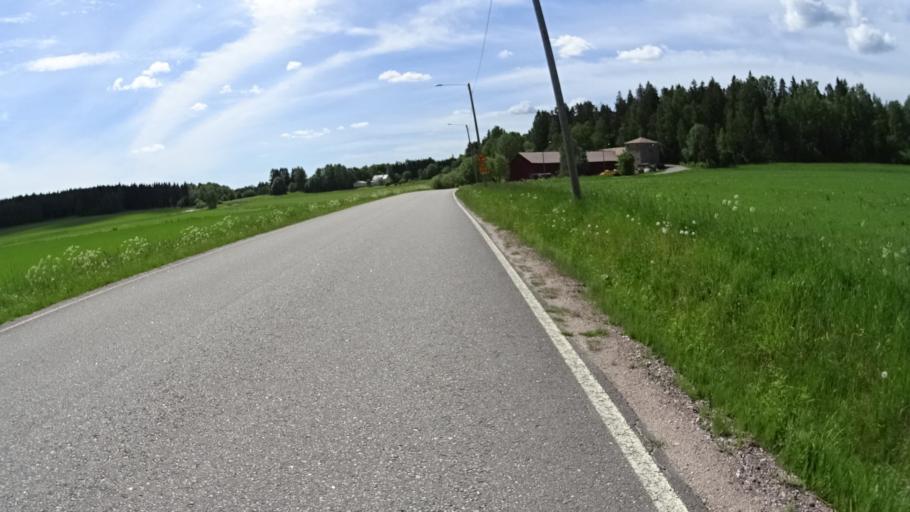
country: FI
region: Uusimaa
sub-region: Helsinki
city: Espoo
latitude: 60.2801
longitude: 24.6730
